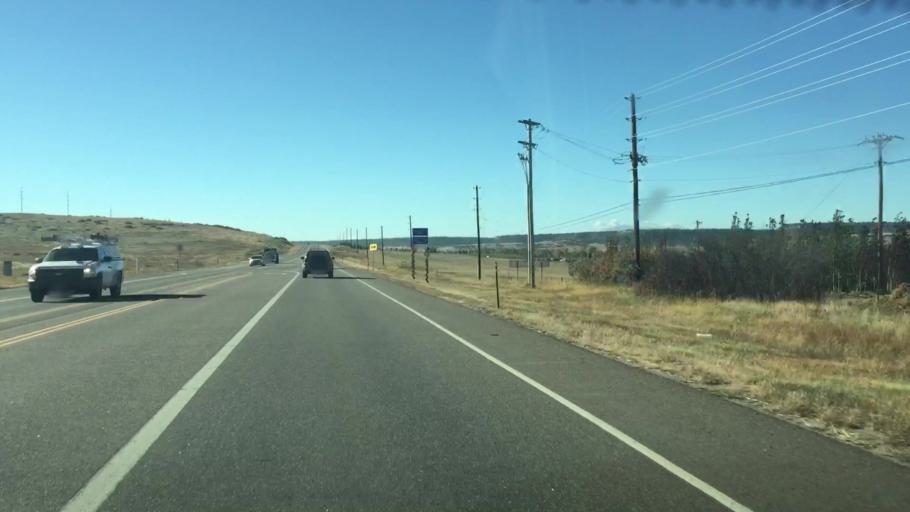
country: US
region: Colorado
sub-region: Douglas County
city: The Pinery
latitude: 39.4281
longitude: -104.7609
